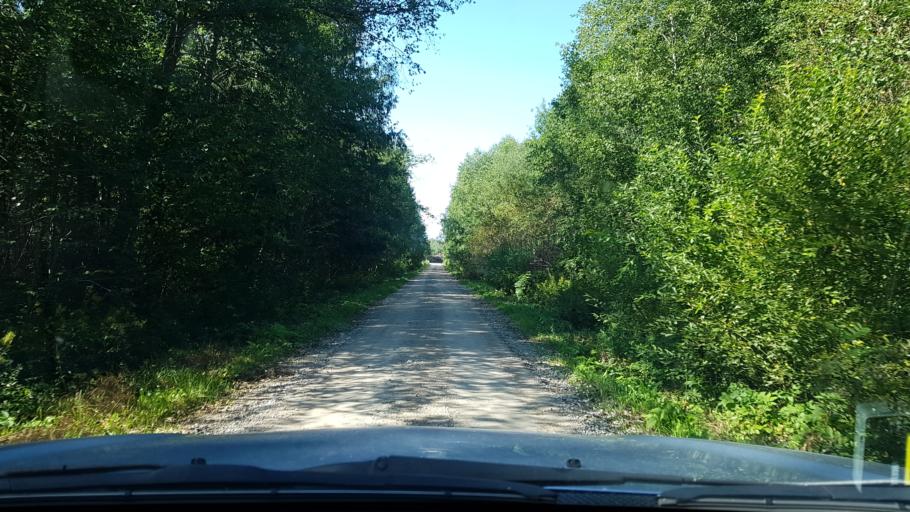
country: EE
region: Ida-Virumaa
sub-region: Sillamaee linn
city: Sillamae
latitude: 59.3321
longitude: 27.7688
